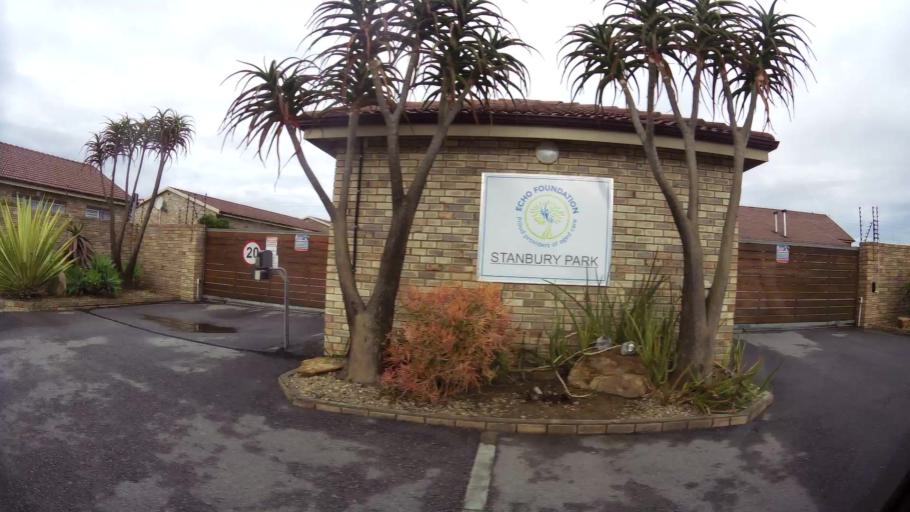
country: ZA
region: Eastern Cape
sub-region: Nelson Mandela Bay Metropolitan Municipality
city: Port Elizabeth
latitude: -33.9706
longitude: 25.6238
